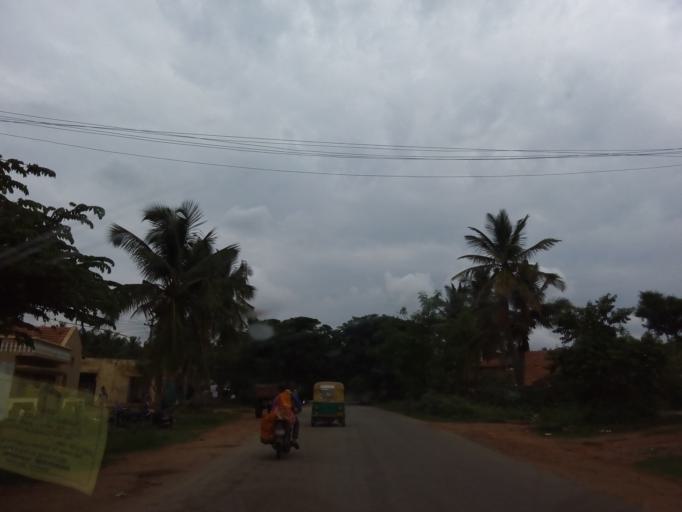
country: IN
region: Karnataka
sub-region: Hassan
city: Channarayapatna
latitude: 12.8827
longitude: 76.4163
